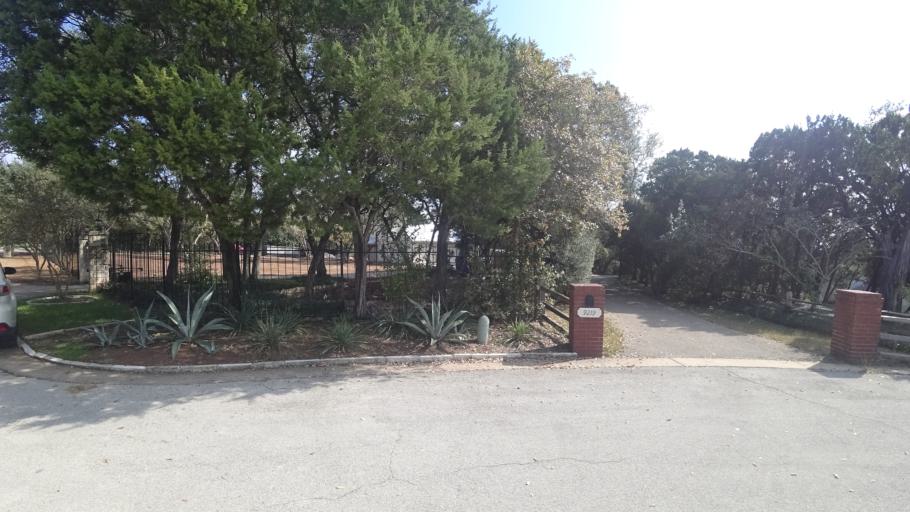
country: US
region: Texas
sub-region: Travis County
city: Barton Creek
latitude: 30.3127
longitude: -97.8730
